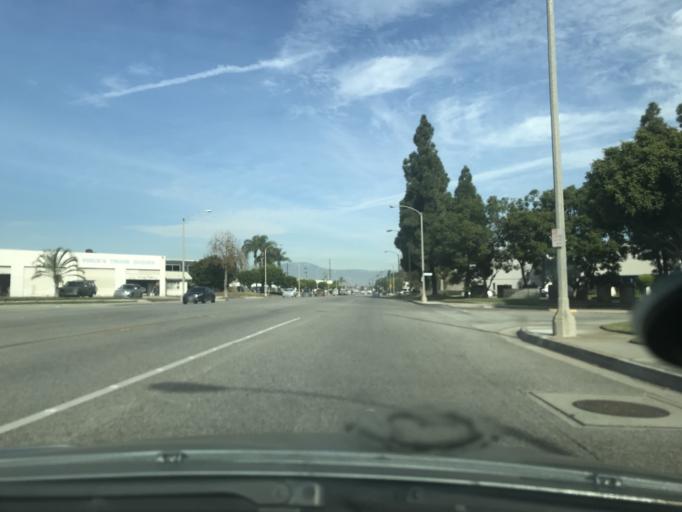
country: US
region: California
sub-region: Los Angeles County
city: Santa Fe Springs
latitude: 33.9541
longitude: -118.0720
